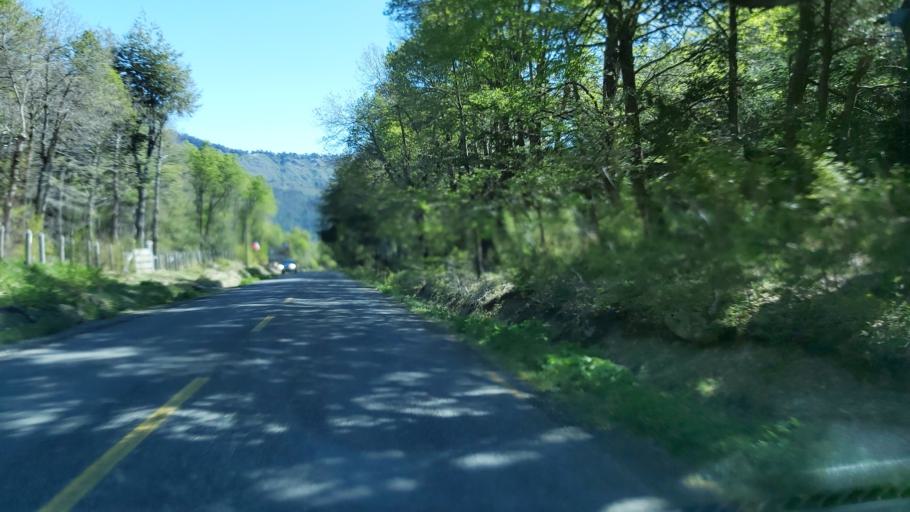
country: CL
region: Araucania
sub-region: Provincia de Cautin
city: Vilcun
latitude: -38.4764
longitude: -71.5322
